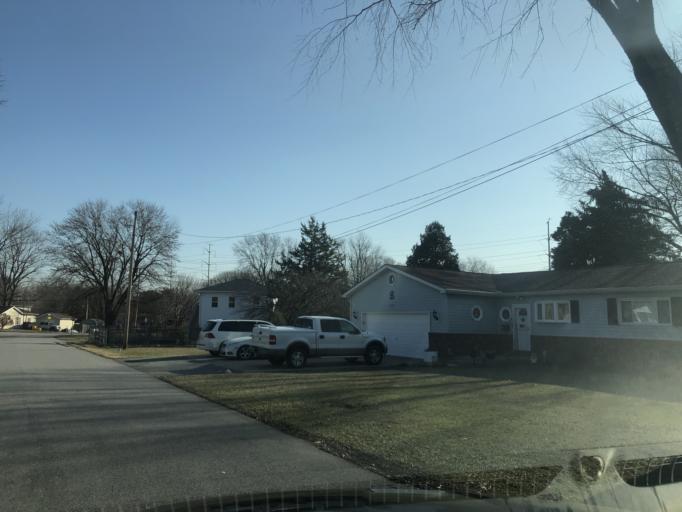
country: US
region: Maryland
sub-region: Anne Arundel County
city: Odenton
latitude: 39.0783
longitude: -76.6949
